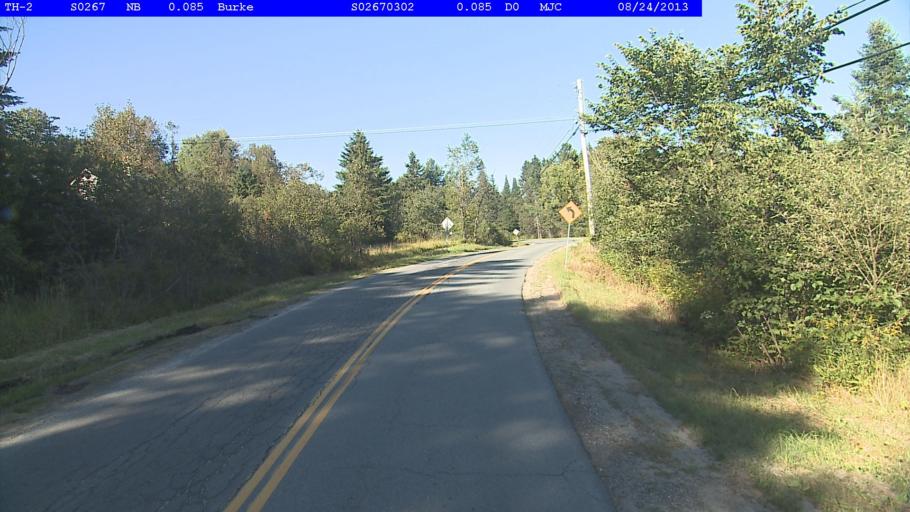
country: US
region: Vermont
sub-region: Caledonia County
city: Lyndonville
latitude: 44.5887
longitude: -71.9470
